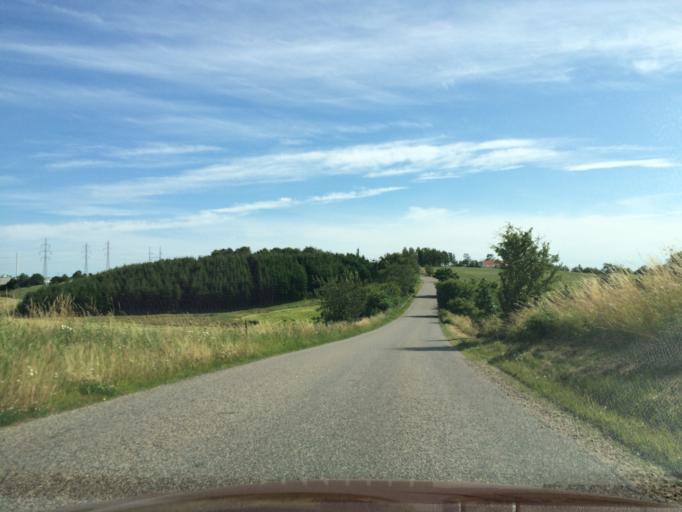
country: DK
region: Central Jutland
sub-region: Silkeborg Kommune
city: Silkeborg
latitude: 56.2126
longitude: 9.5622
